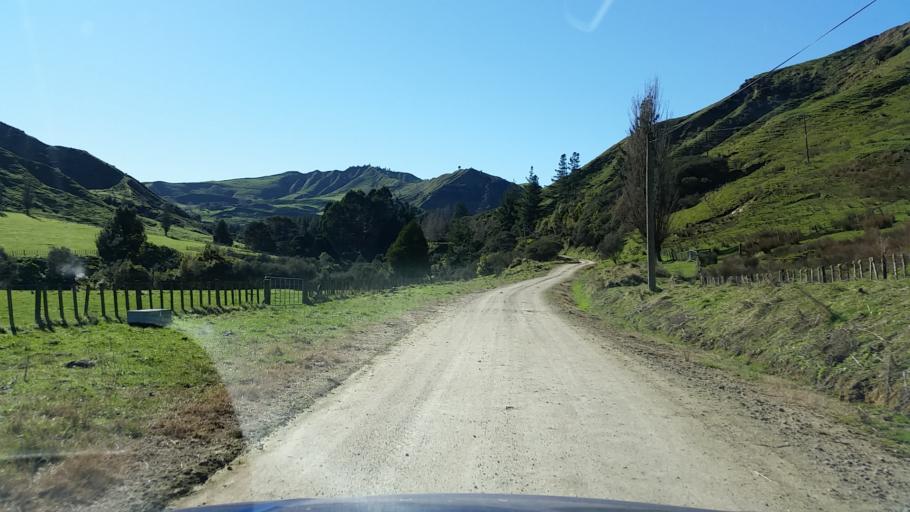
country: NZ
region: Manawatu-Wanganui
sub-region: Wanganui District
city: Wanganui
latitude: -39.5372
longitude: 174.9202
